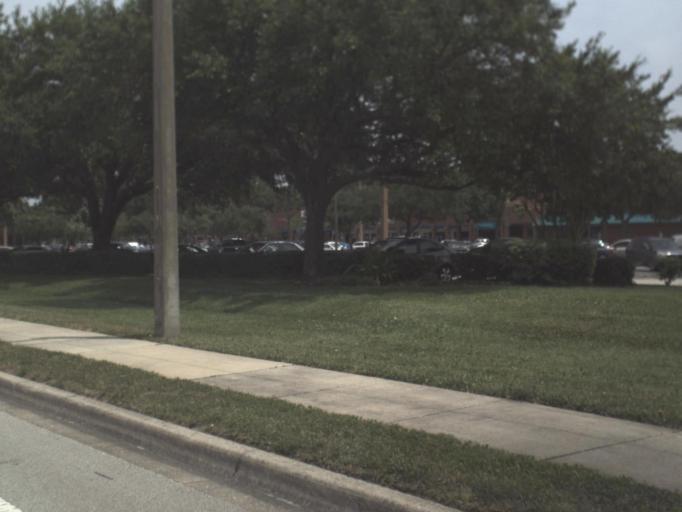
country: US
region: Florida
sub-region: Duval County
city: Atlantic Beach
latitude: 30.3199
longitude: -81.4623
